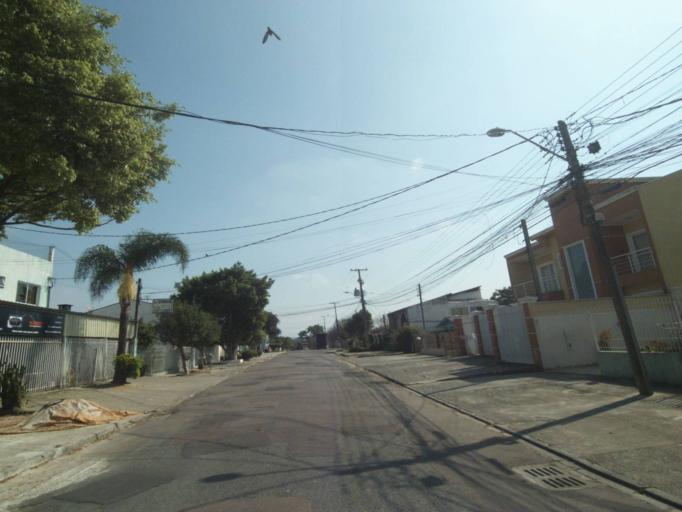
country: BR
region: Parana
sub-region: Curitiba
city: Curitiba
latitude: -25.4830
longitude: -49.3300
